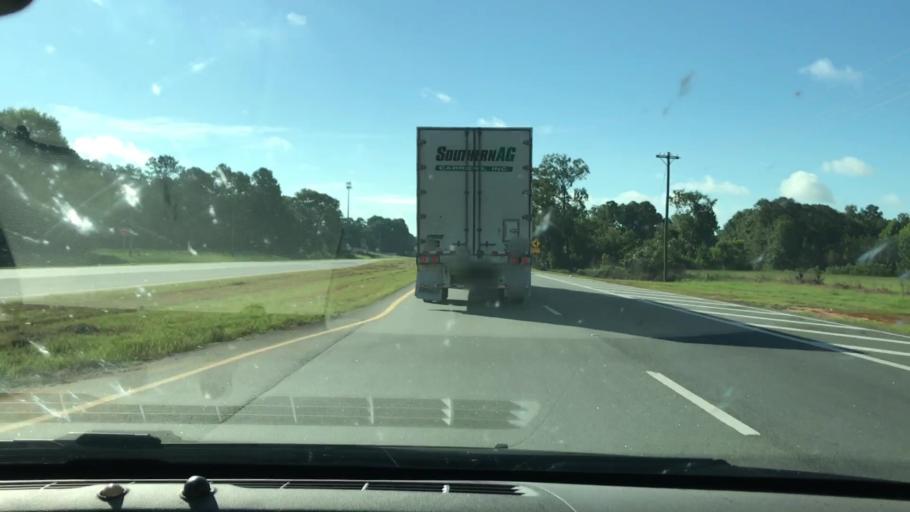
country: US
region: Georgia
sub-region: Lee County
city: Leesburg
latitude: 31.6638
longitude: -84.2801
